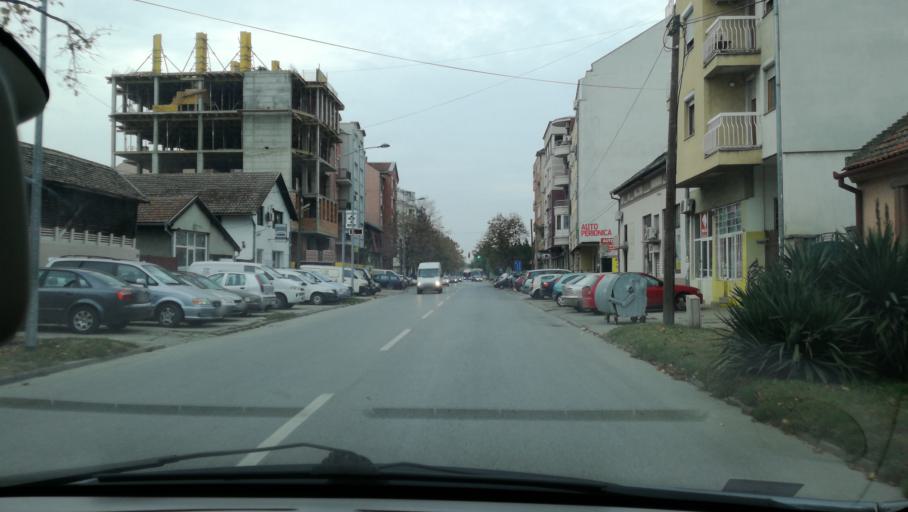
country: RS
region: Autonomna Pokrajina Vojvodina
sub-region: Juznobacki Okrug
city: Novi Sad
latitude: 45.2636
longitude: 19.8385
